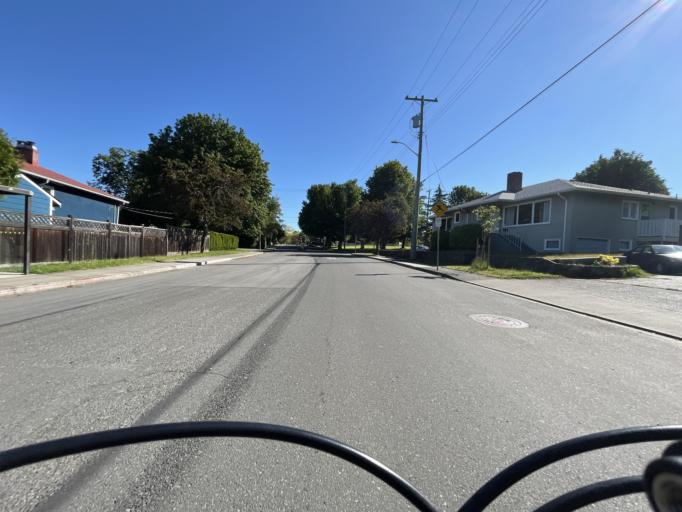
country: CA
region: British Columbia
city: Oak Bay
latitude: 48.4182
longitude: -123.3300
